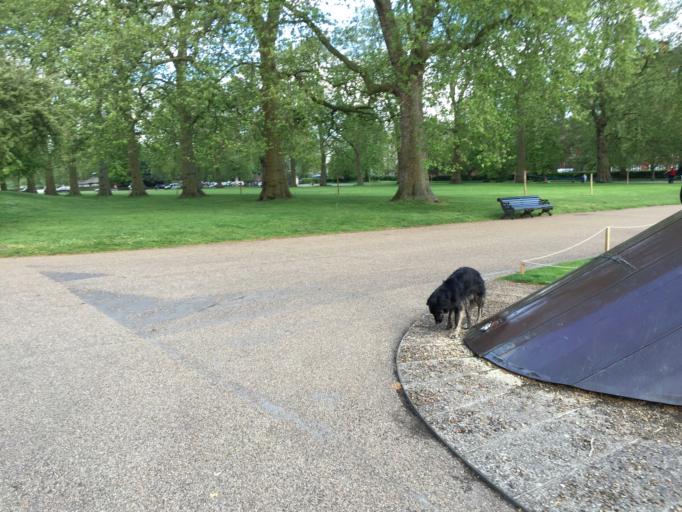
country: GB
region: England
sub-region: Greater London
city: Bayswater
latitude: 51.5029
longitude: -0.1772
